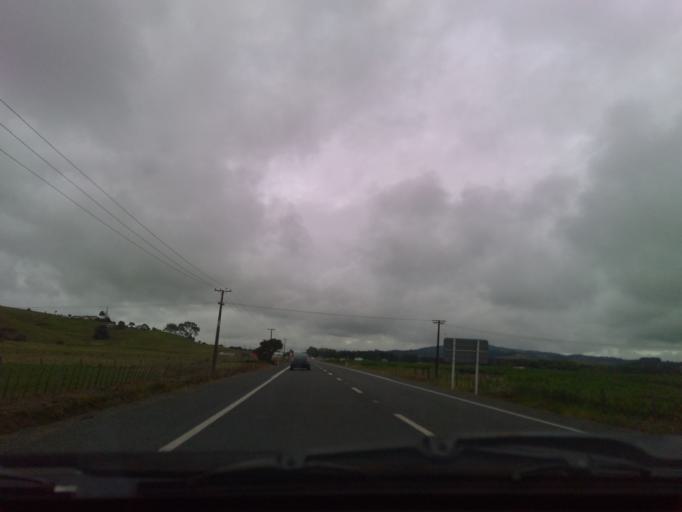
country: NZ
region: Northland
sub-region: Whangarei
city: Ruakaka
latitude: -35.8955
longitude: 174.4380
